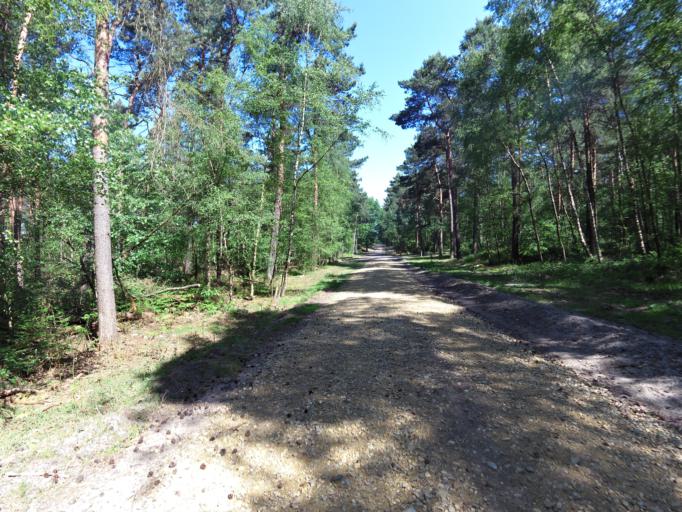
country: NL
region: Limburg
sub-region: Gemeente Onderbanken
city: Schinveld
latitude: 50.9435
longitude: 6.0335
